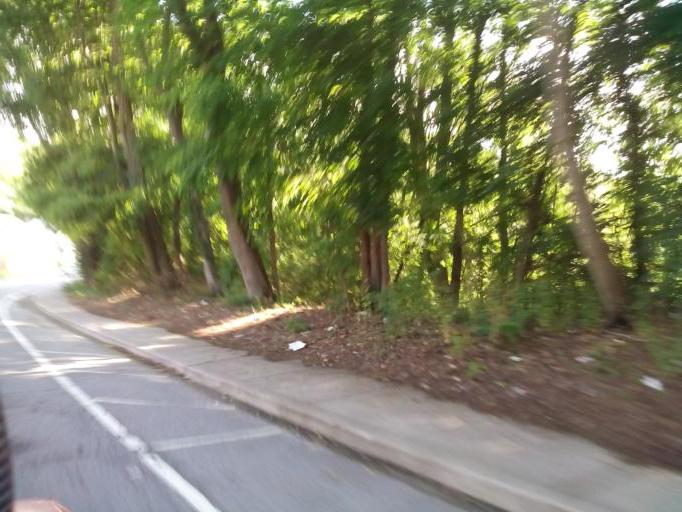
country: US
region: New York
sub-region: Nassau County
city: Oyster Bay
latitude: 40.8687
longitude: -73.5398
